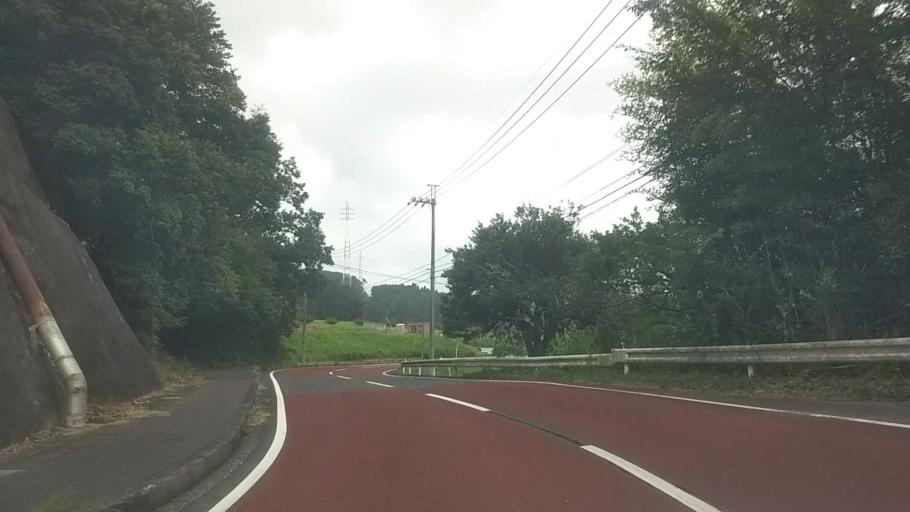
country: JP
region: Chiba
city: Kawaguchi
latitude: 35.2472
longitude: 140.0781
